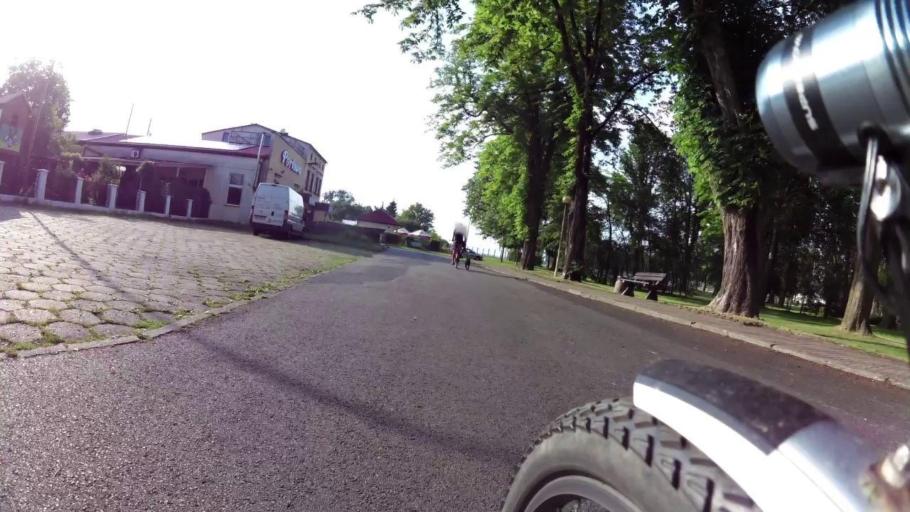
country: PL
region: West Pomeranian Voivodeship
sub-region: Powiat goleniowski
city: Stepnica
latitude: 53.6596
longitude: 14.5175
